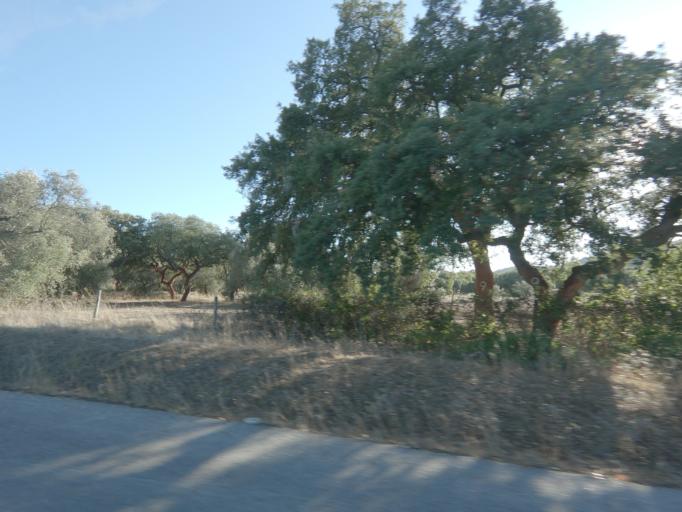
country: PT
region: Setubal
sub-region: Palmela
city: Quinta do Anjo
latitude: 38.5171
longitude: -8.9808
